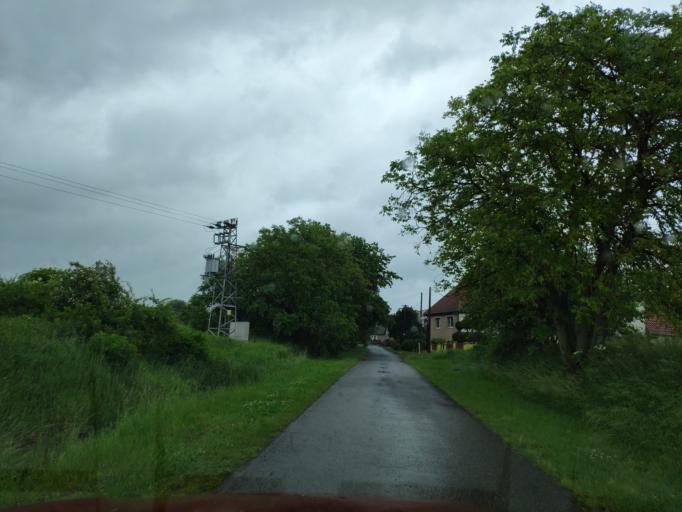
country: SK
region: Kosicky
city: Cierna nad Tisou
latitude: 48.4260
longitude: 22.1048
